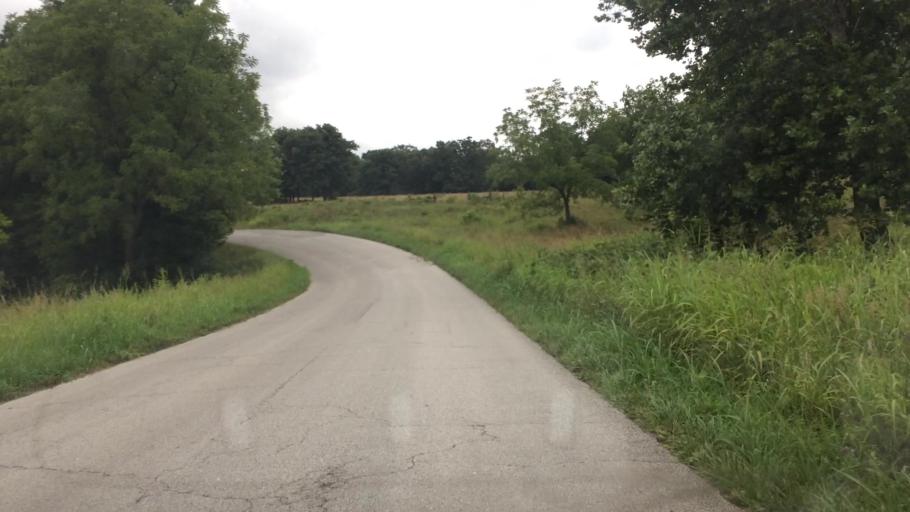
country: US
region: Missouri
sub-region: Greene County
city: Strafford
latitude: 37.3085
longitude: -93.0700
